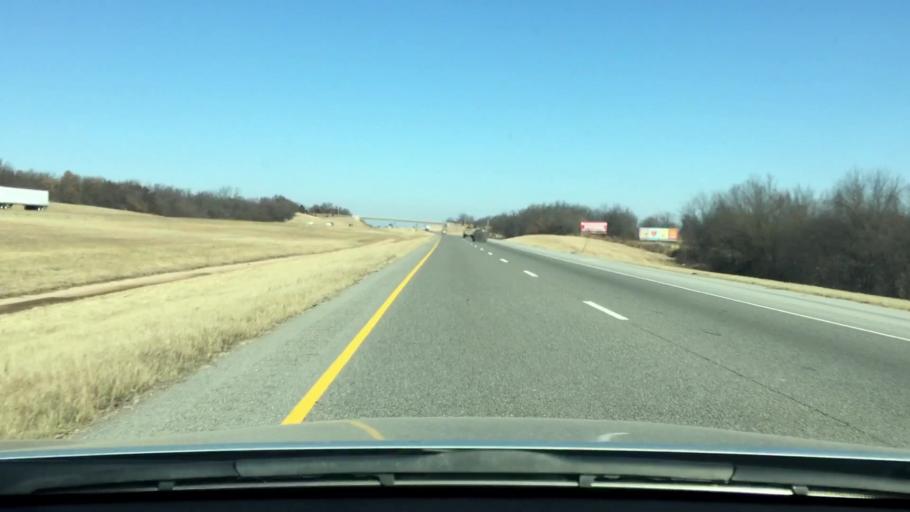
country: US
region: Oklahoma
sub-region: McClain County
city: Purcell
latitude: 34.9509
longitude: -97.3685
